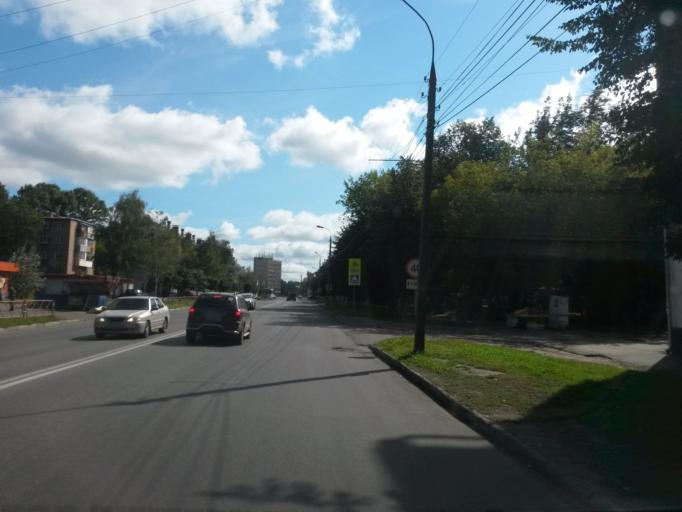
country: RU
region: Jaroslavl
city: Yaroslavl
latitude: 57.6303
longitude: 39.8420
